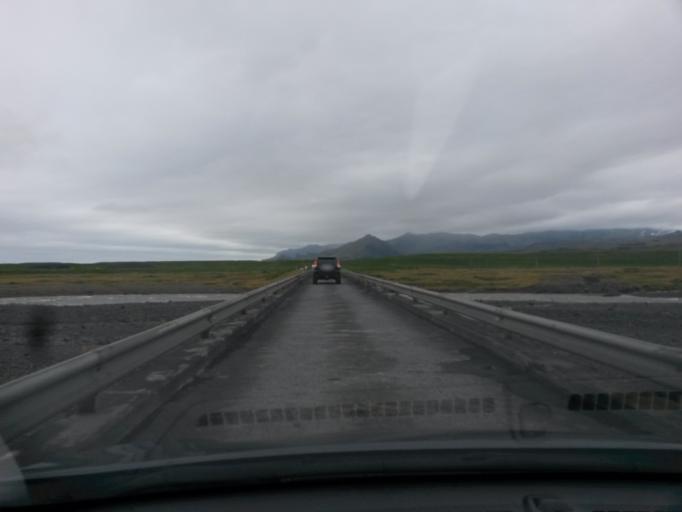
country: IS
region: South
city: Vestmannaeyjar
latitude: 63.4984
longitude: -19.3996
